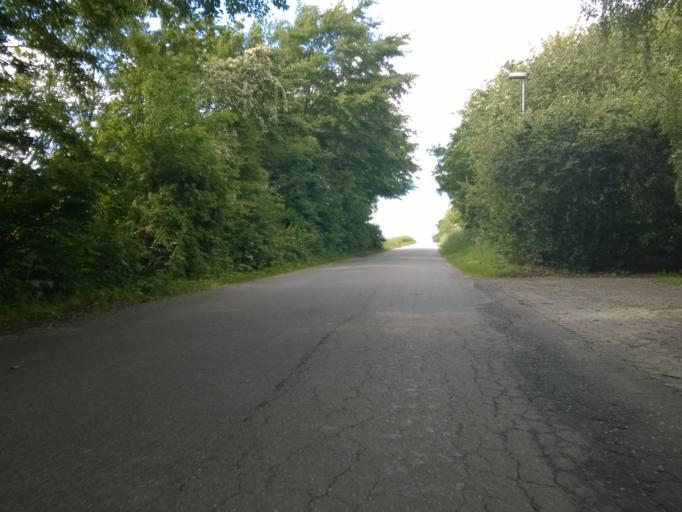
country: DK
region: Central Jutland
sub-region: Holstebro Kommune
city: Vinderup
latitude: 56.4862
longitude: 8.8384
